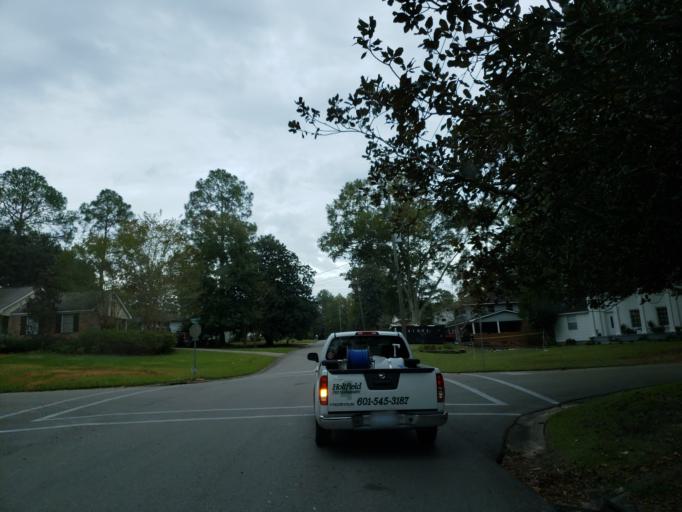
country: US
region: Mississippi
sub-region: Lamar County
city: West Hattiesburg
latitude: 31.3144
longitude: -89.3349
